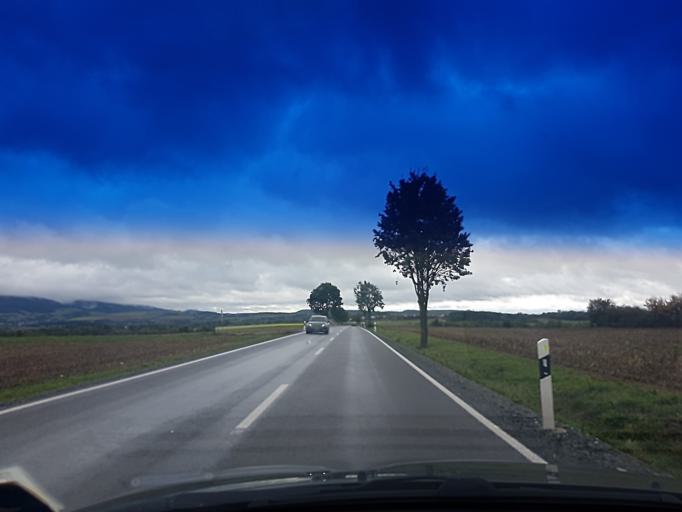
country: DE
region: Bavaria
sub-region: Upper Franconia
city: Bindlach
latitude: 50.0120
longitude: 11.6132
